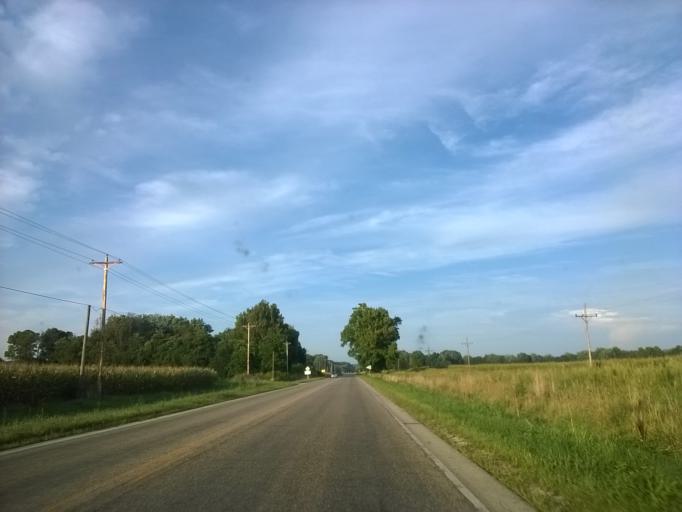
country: US
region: Indiana
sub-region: Morgan County
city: Martinsville
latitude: 39.4170
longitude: -86.4826
